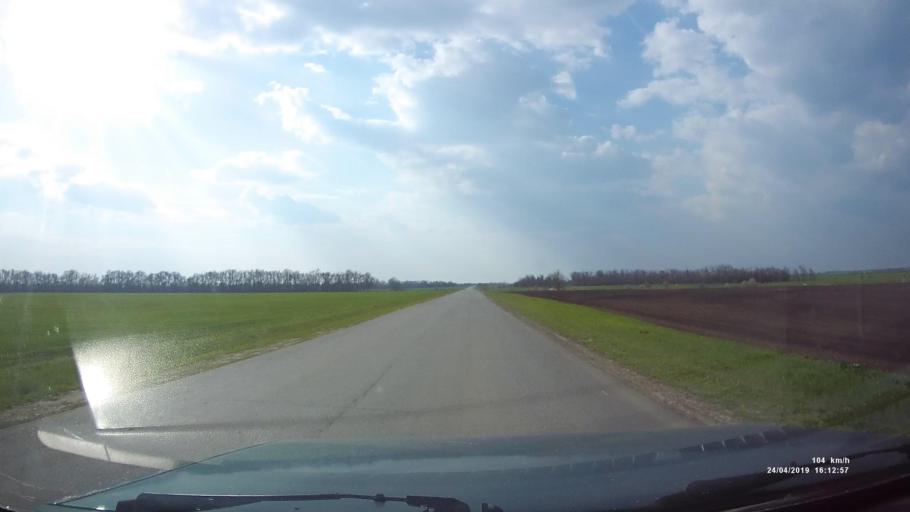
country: RU
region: Rostov
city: Sovetskoye
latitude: 46.7371
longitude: 42.2281
